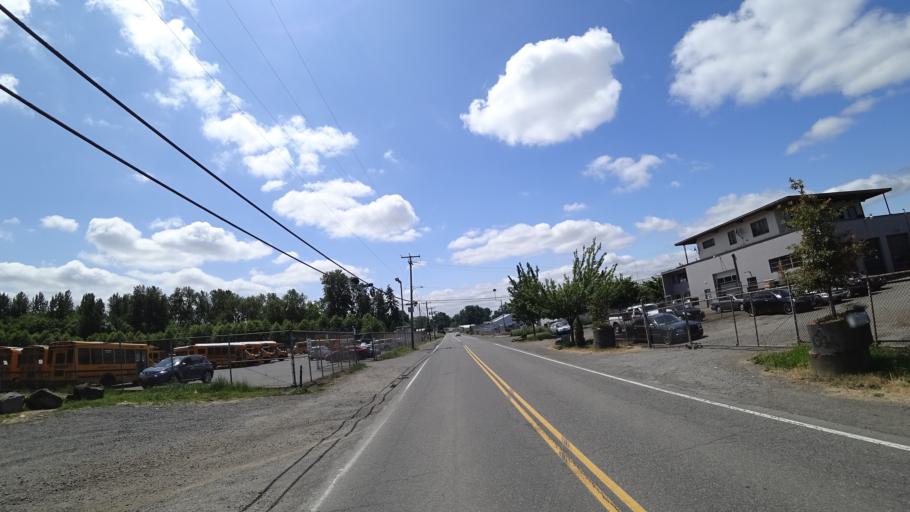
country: US
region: Washington
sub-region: Clark County
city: Vancouver
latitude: 45.5961
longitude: -122.6620
